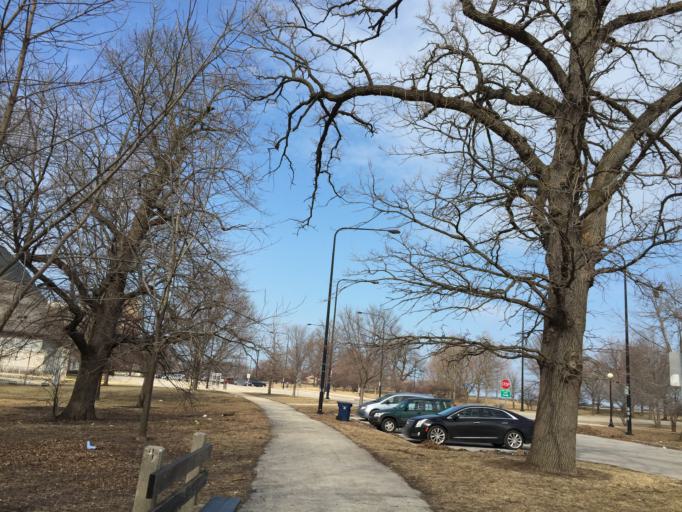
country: US
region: Illinois
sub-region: Cook County
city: Chicago
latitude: 41.7893
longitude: -87.5808
